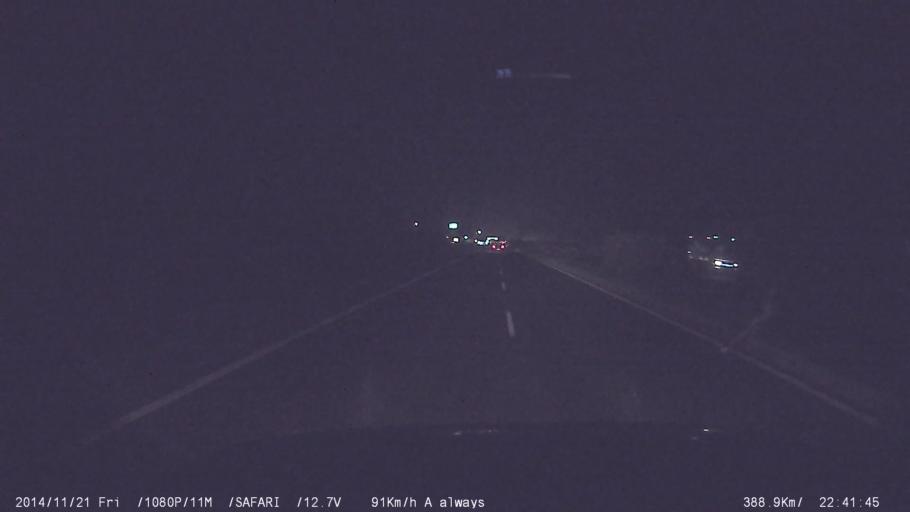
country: IN
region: Tamil Nadu
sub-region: Villupuram
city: Tindivanam
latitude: 12.2460
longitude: 79.6681
